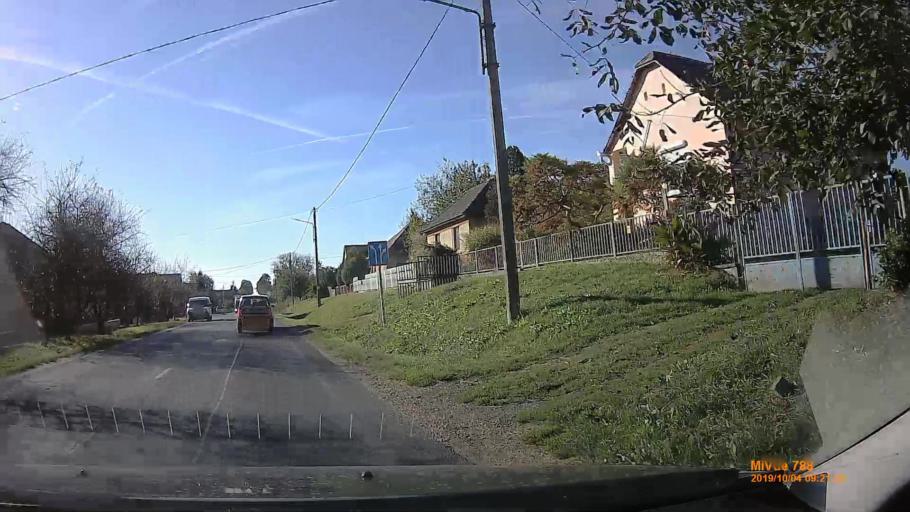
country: HU
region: Somogy
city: Karad
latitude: 46.5538
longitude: 17.8116
